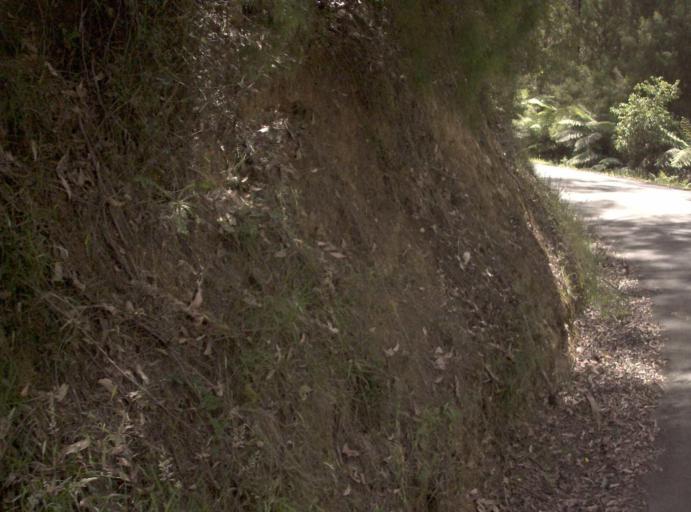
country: AU
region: Victoria
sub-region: Latrobe
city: Moe
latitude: -37.8359
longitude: 146.1635
